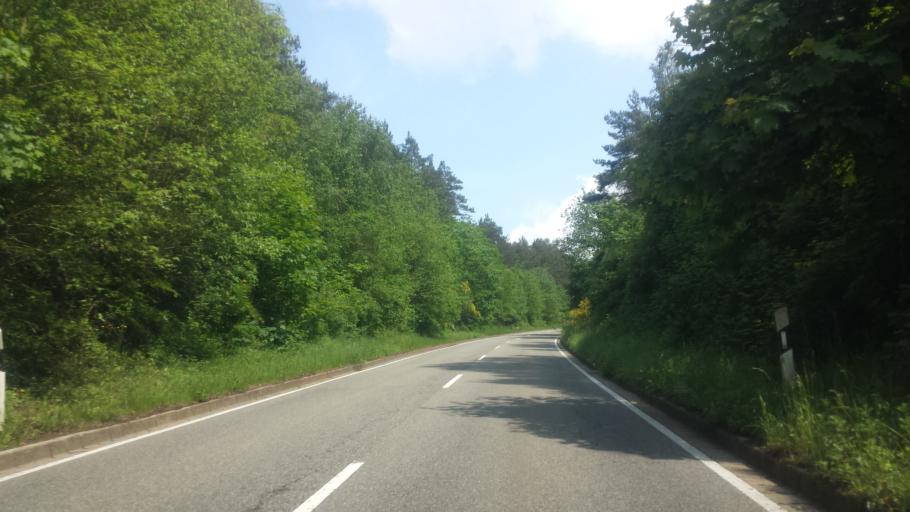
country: DE
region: Rheinland-Pfalz
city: Lindenberg
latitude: 49.3762
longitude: 8.0966
